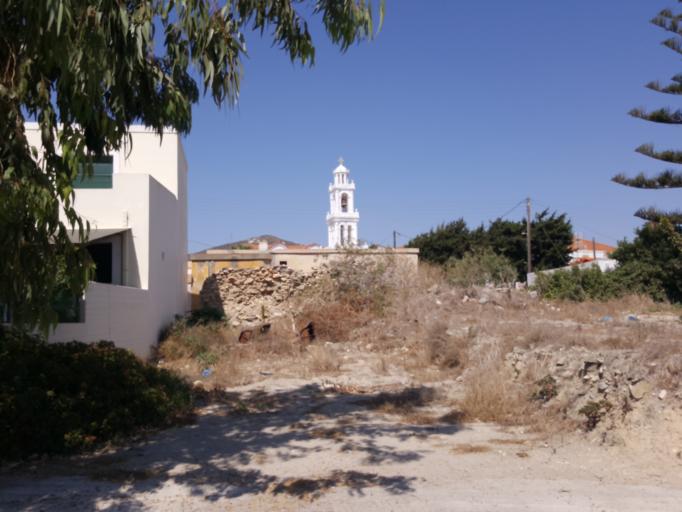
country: GR
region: South Aegean
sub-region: Nomos Dodekanisou
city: Lardos
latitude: 35.9533
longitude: 27.7689
